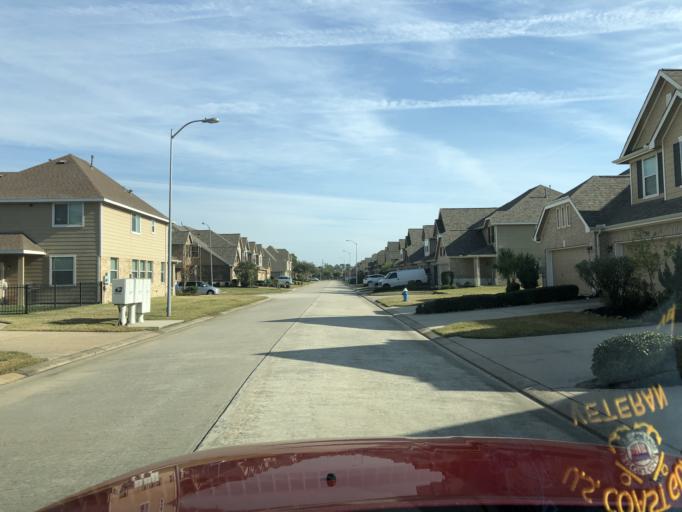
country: US
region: Texas
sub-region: Harris County
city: Tomball
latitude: 30.0364
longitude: -95.5544
